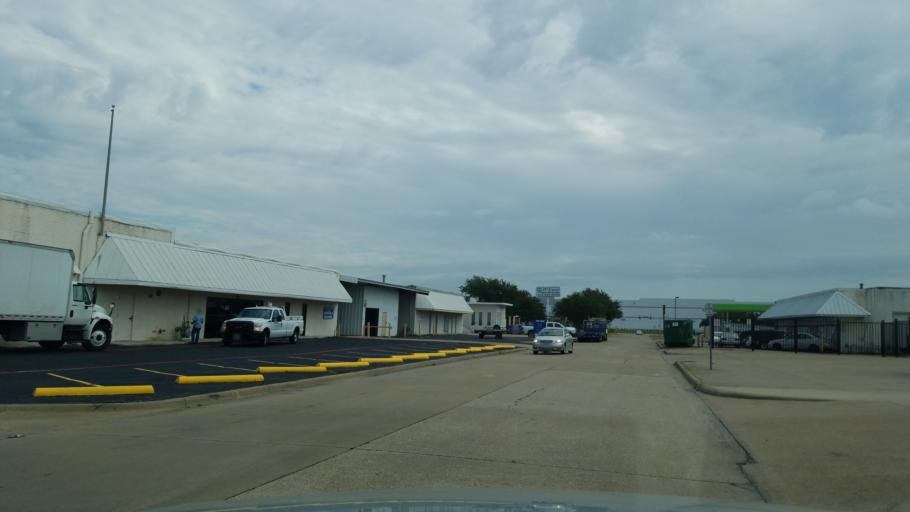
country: US
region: Texas
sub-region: Dallas County
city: Garland
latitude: 32.8973
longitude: -96.6859
